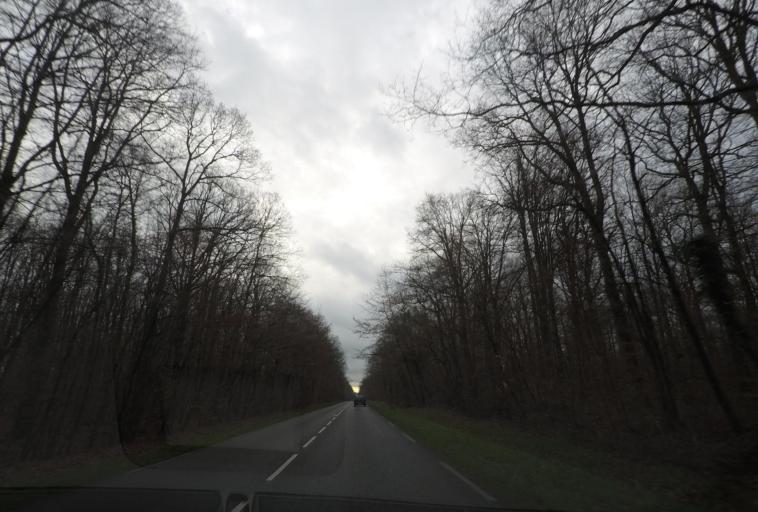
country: FR
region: Pays de la Loire
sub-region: Departement de la Sarthe
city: Vibraye
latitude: 48.0322
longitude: 0.7472
